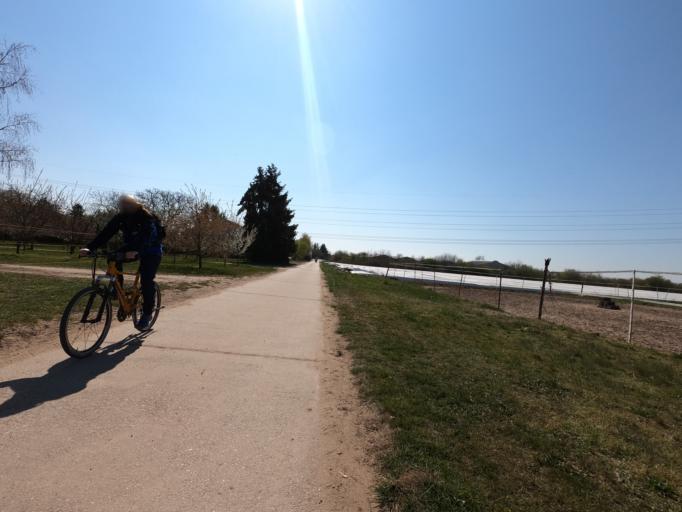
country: DE
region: Hesse
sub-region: Regierungsbezirk Darmstadt
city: Buttelborn
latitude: 49.9288
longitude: 8.5161
